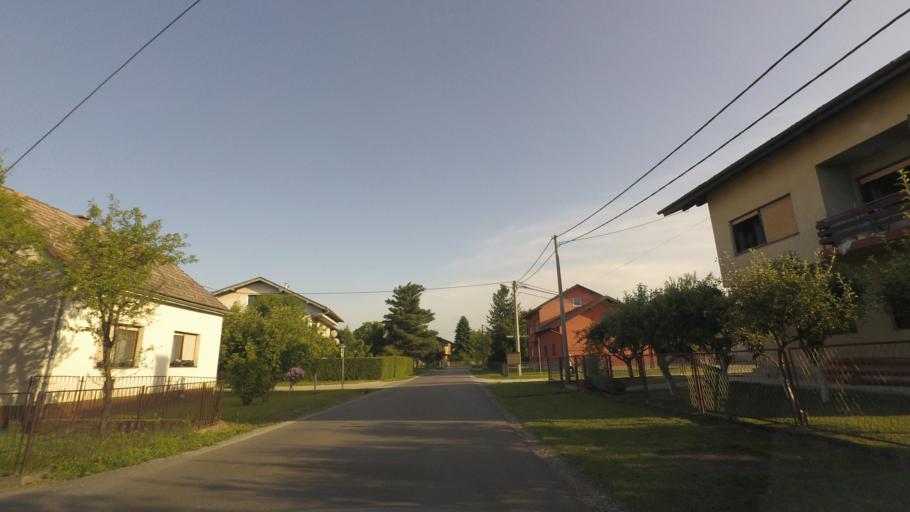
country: HR
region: Karlovacka
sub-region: Grad Karlovac
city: Karlovac
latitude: 45.5089
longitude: 15.5311
